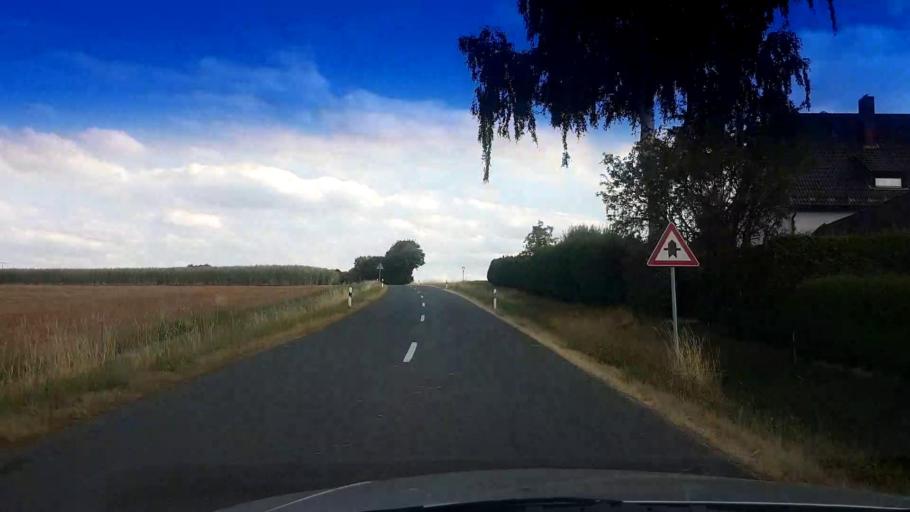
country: DE
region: Bavaria
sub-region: Upper Palatinate
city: Waldsassen
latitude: 50.0161
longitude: 12.3605
